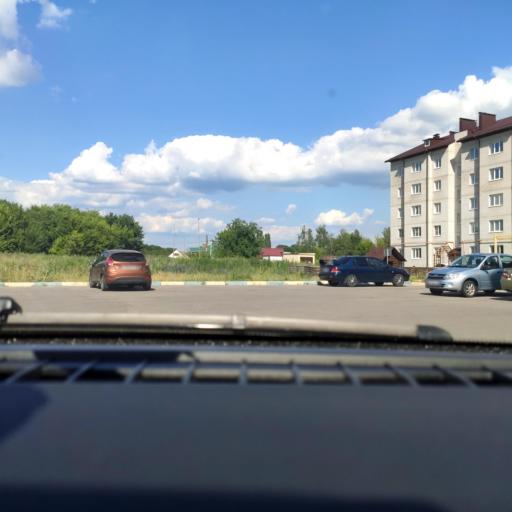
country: RU
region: Voronezj
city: Ramon'
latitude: 51.8278
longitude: 39.2654
